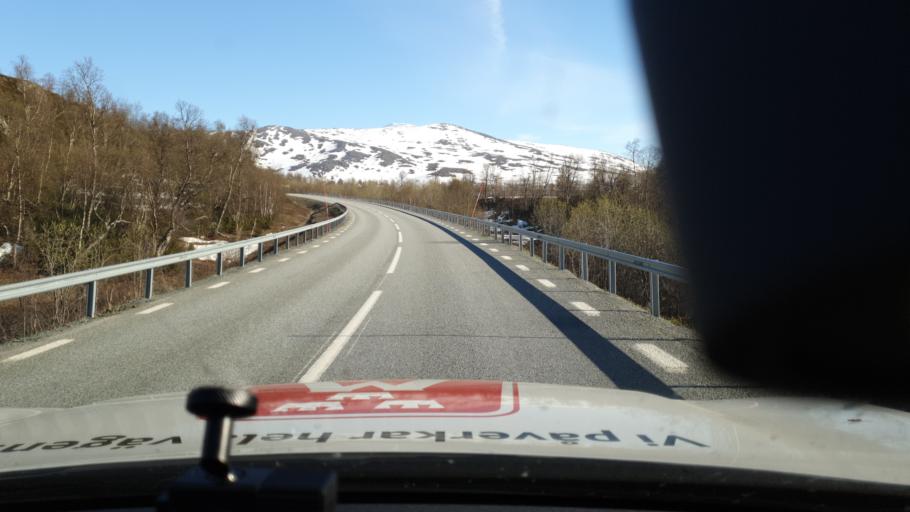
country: NO
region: Nordland
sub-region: Rana
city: Mo i Rana
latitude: 66.0592
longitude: 14.8725
